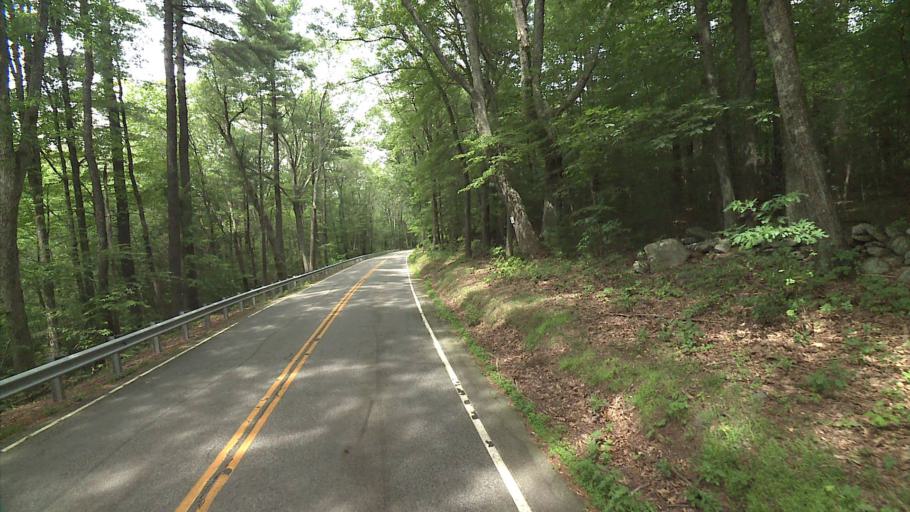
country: US
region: Massachusetts
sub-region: Hampden County
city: Holland
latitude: 41.9671
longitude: -72.1118
